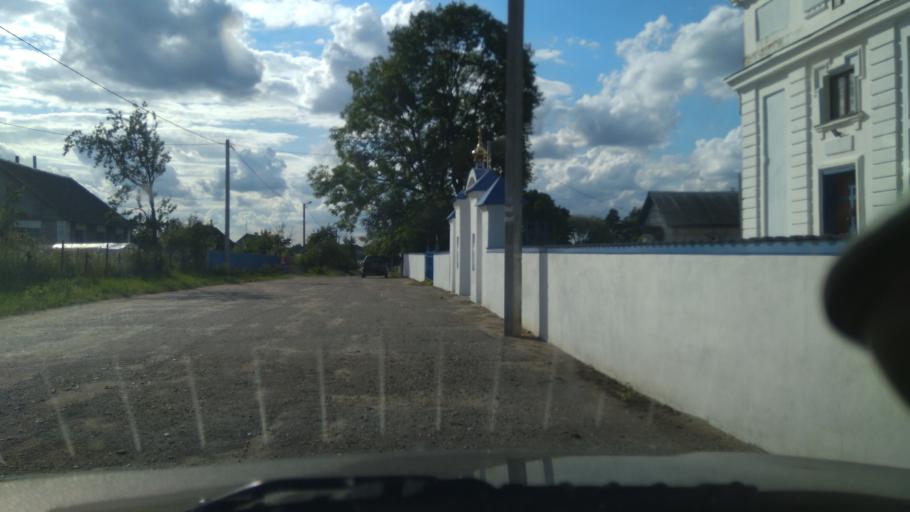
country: BY
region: Grodnenskaya
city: Masty
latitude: 53.3141
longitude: 24.6999
